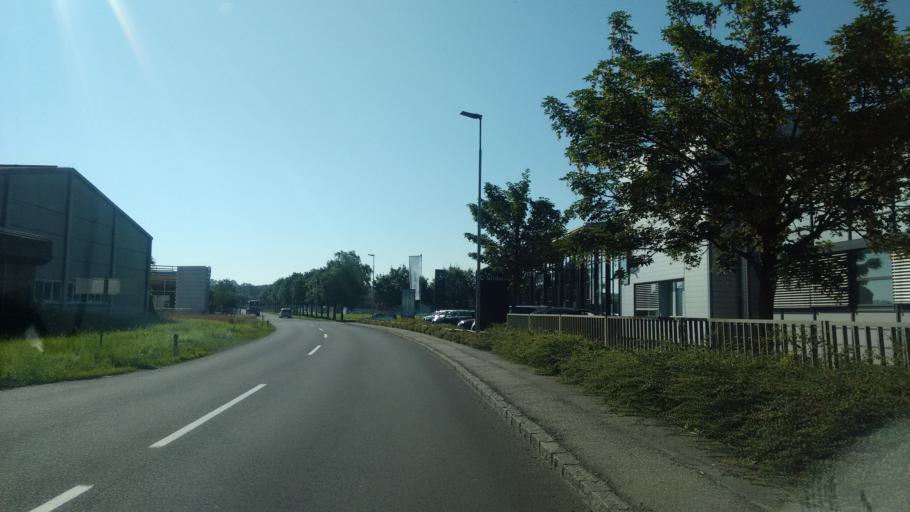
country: AT
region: Upper Austria
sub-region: Wels-Land
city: Gunskirchen
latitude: 48.1341
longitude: 13.9522
